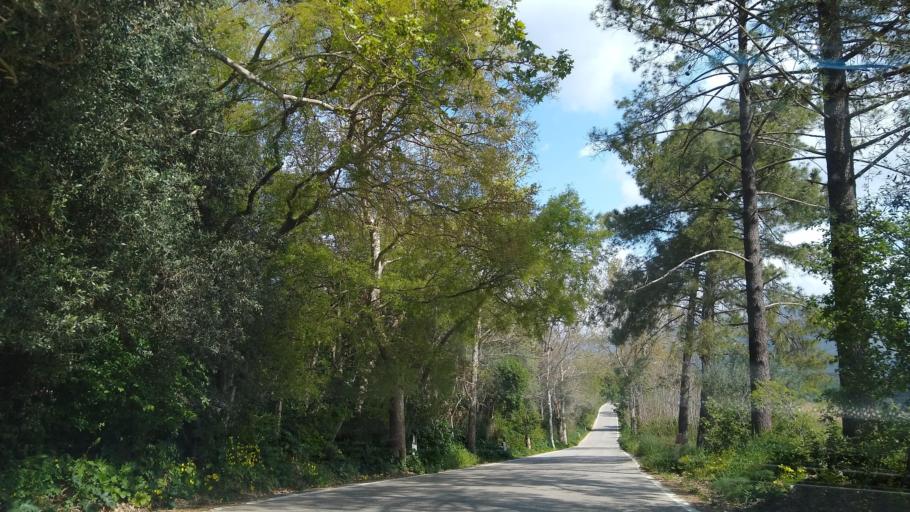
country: IT
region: Sicily
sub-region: Trapani
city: Calatafimi
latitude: 37.9367
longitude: 12.8507
